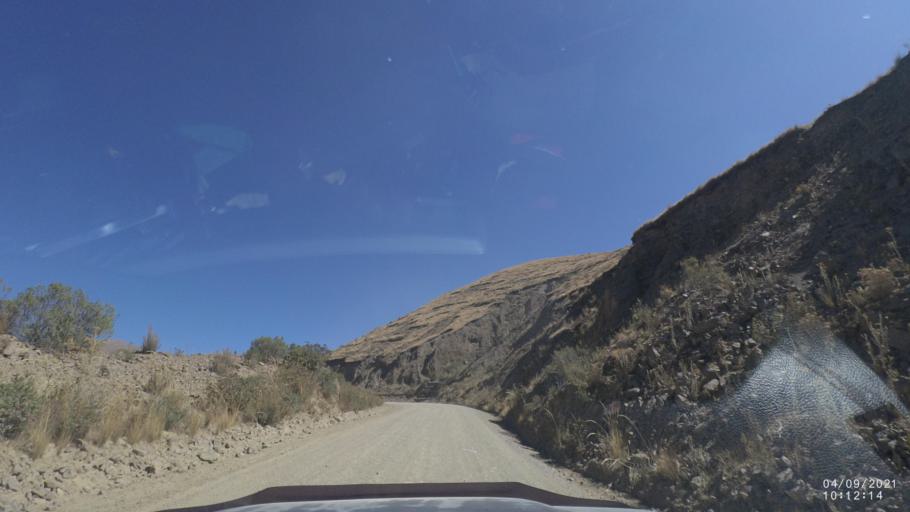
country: BO
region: Cochabamba
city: Sipe Sipe
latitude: -17.3416
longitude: -66.3988
